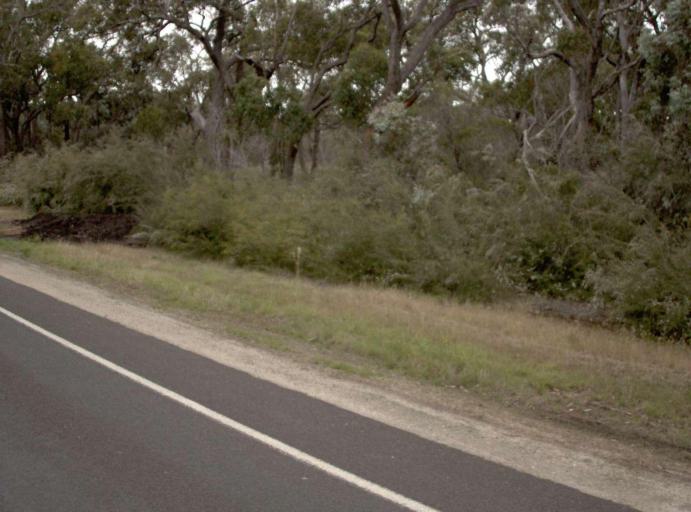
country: AU
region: Victoria
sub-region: Wellington
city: Sale
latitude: -38.3351
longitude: 147.0140
